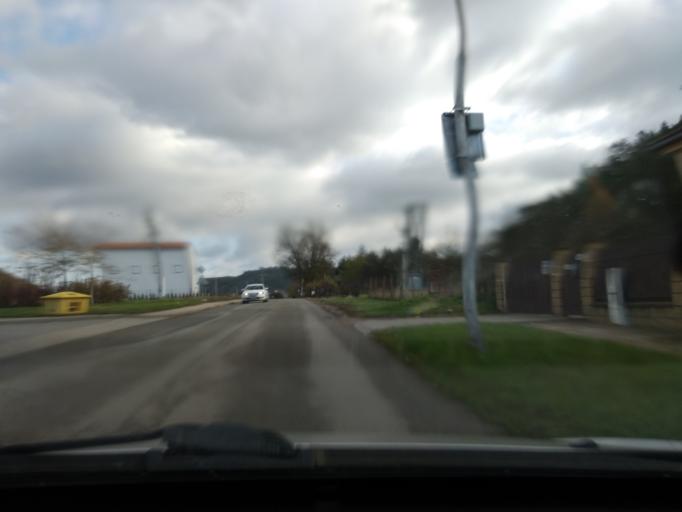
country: CZ
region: South Moravian
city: Tisnov
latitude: 49.3501
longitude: 16.4333
